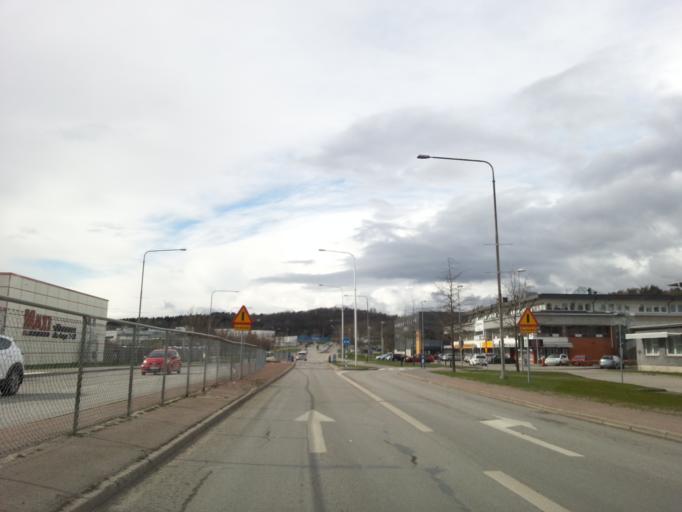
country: SE
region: Vaestra Goetaland
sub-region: Kungalvs Kommun
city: Kungalv
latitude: 57.8747
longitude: 11.9759
